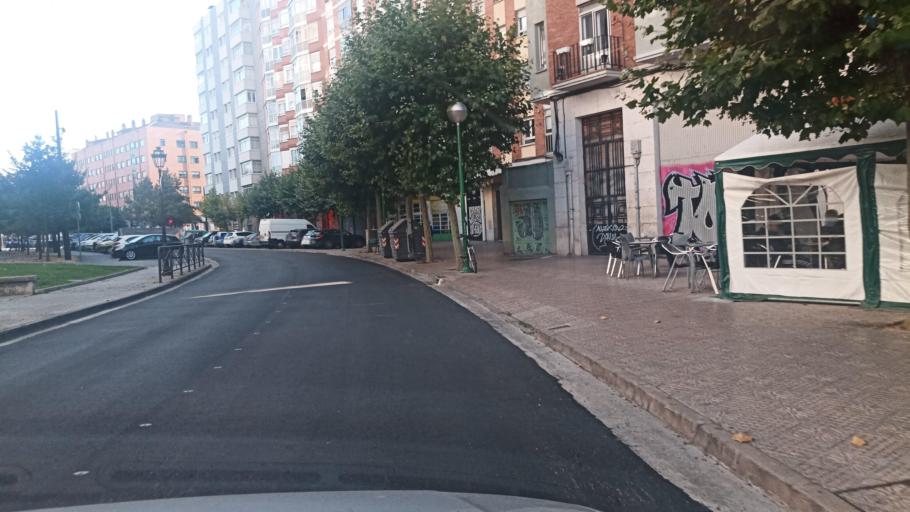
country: ES
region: Castille and Leon
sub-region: Provincia de Burgos
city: Burgos
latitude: 42.3372
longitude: -3.6971
